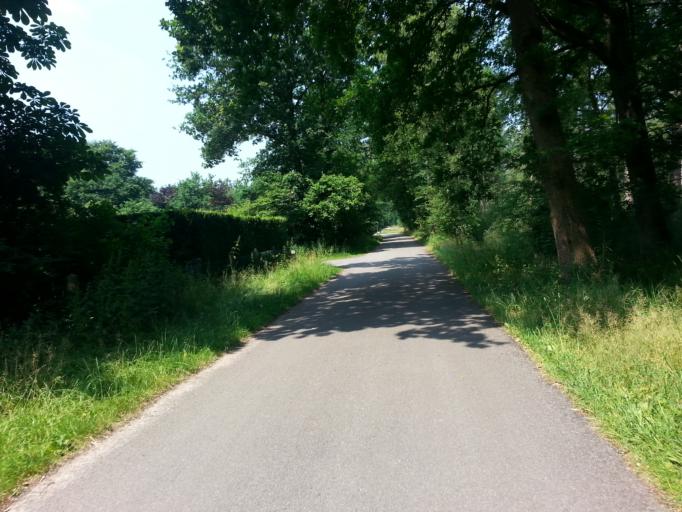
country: NL
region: Utrecht
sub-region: Gemeente Amersfoort
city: Randenbroek
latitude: 52.1245
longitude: 5.3918
